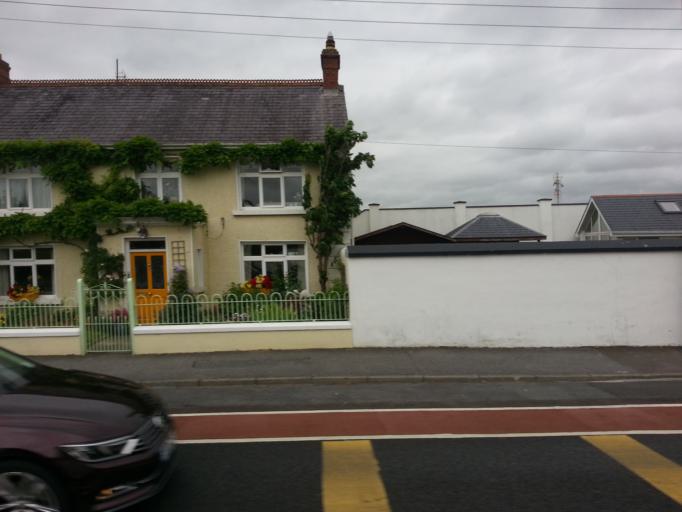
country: IE
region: Leinster
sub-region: Kilkenny
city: Kilkenny
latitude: 52.6508
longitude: -7.2347
